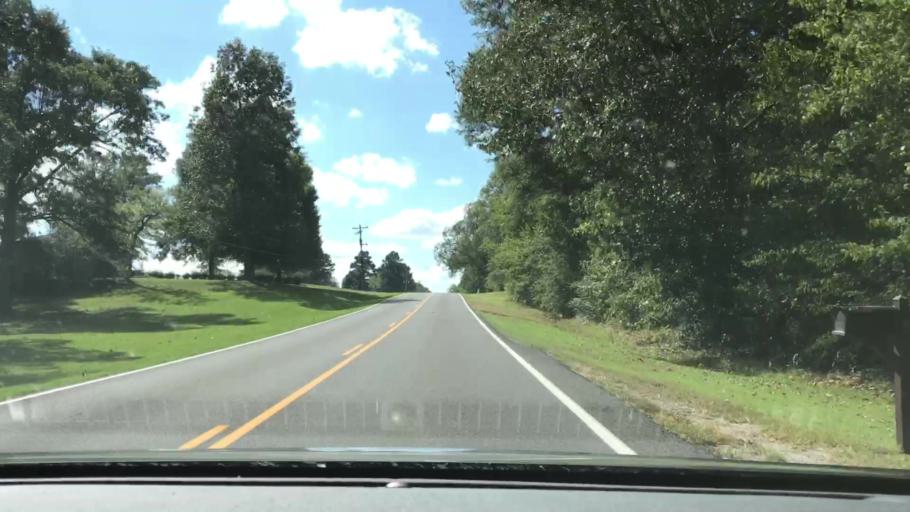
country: US
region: Kentucky
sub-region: McCracken County
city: Reidland
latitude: 36.9073
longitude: -88.5242
